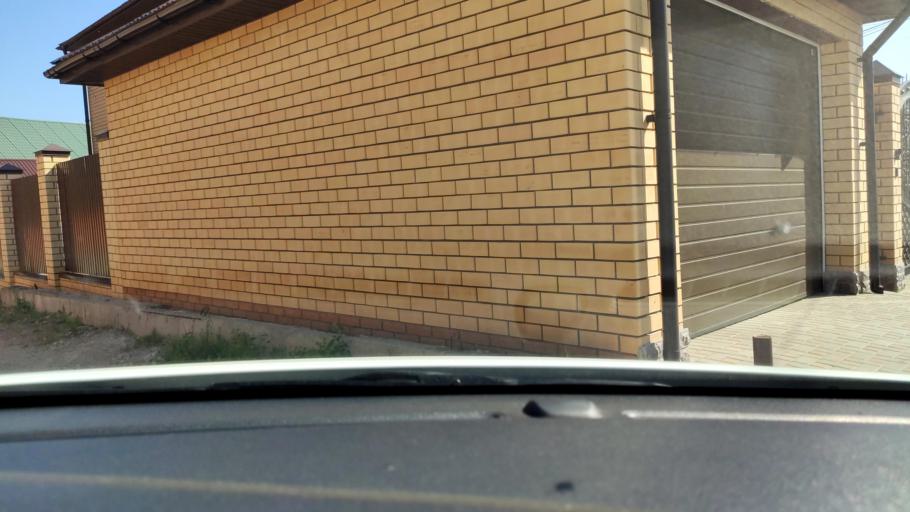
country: RU
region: Tatarstan
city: Stolbishchi
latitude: 55.7420
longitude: 49.2434
